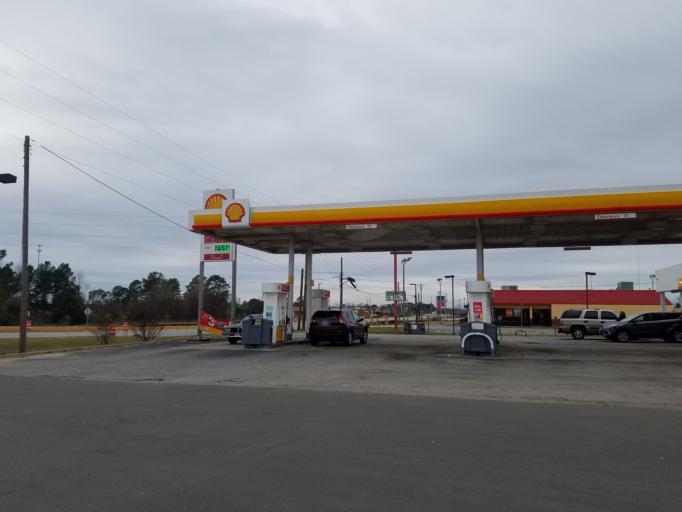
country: US
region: Georgia
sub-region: Dooly County
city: Vienna
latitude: 32.0872
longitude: -83.7650
